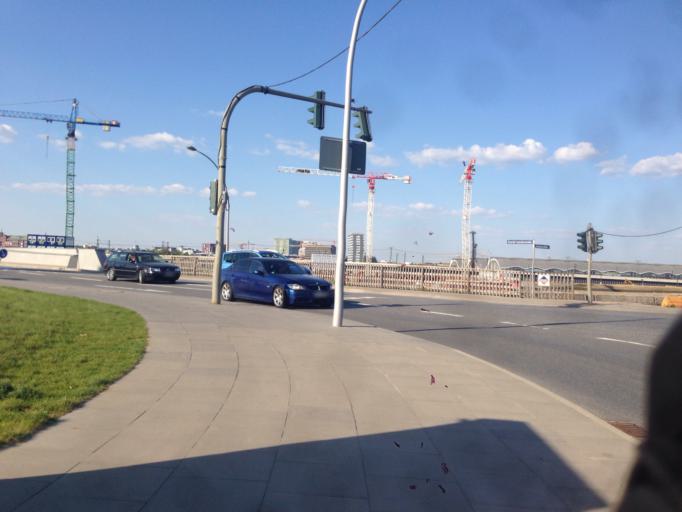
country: DE
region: Hamburg
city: Hamburg-Mitte
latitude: 53.5381
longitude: 10.0084
